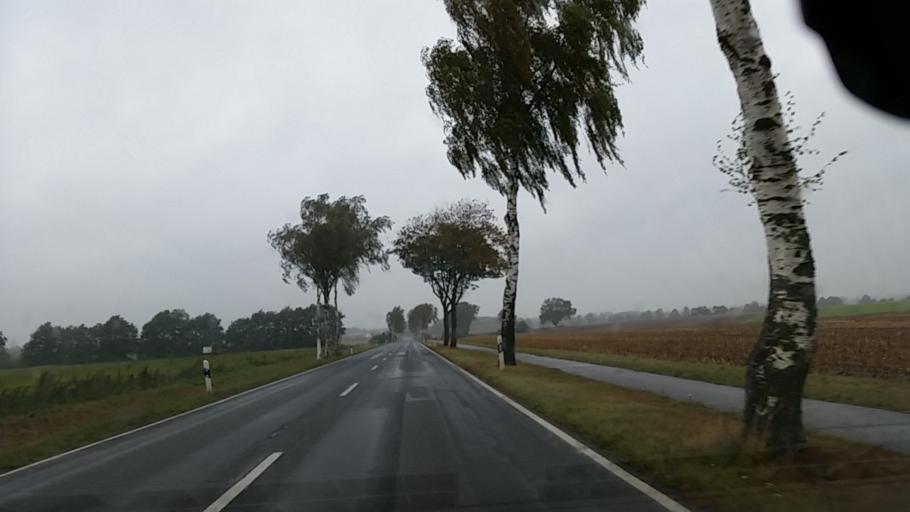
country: DE
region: Lower Saxony
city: Bodenteich
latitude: 52.8182
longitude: 10.6925
